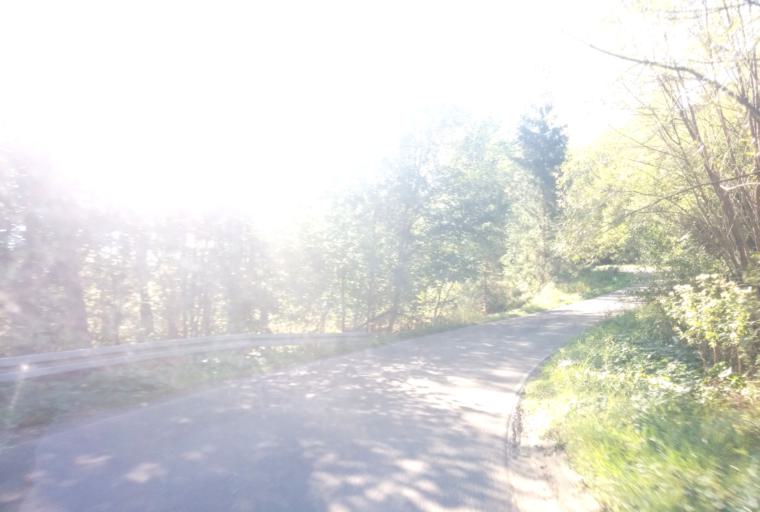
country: PL
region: Subcarpathian Voivodeship
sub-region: Powiat leski
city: Polanczyk
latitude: 49.2734
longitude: 22.4072
